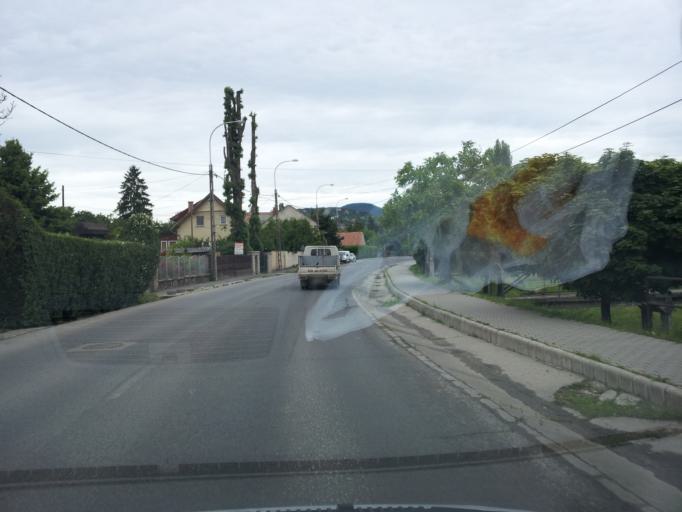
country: HU
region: Pest
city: Pomaz
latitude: 47.6447
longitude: 19.0281
